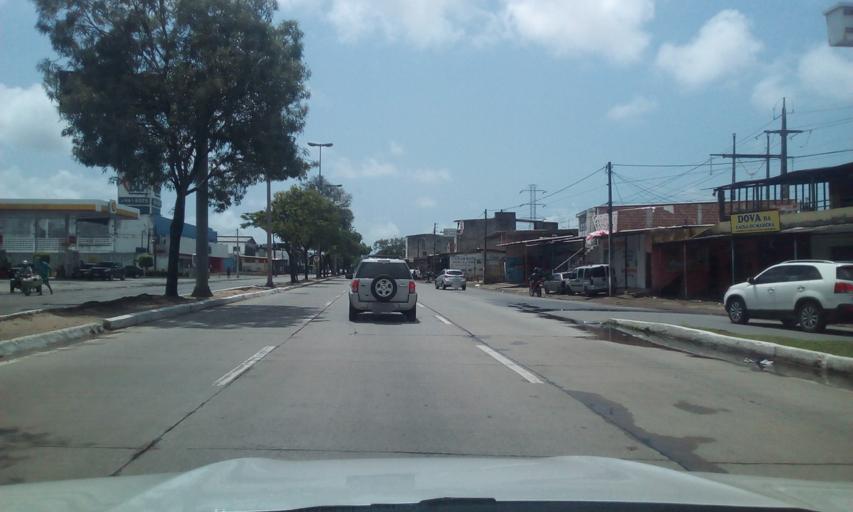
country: BR
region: Pernambuco
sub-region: Recife
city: Recife
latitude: -8.0652
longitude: -34.9383
